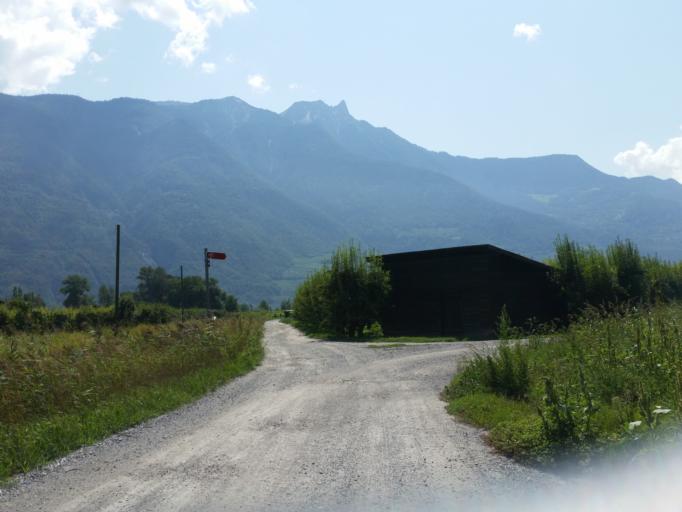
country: CH
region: Valais
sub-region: Martigny District
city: Leytron
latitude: 46.1791
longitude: 7.2014
